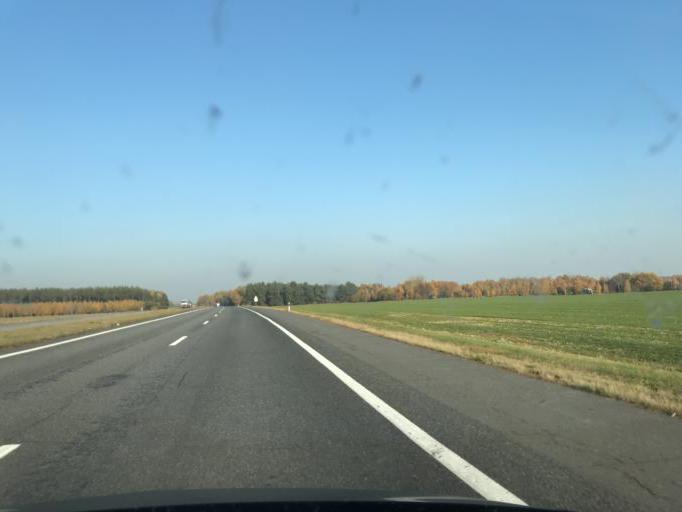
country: BY
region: Minsk
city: Haradzyeya
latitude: 53.4089
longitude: 26.5609
